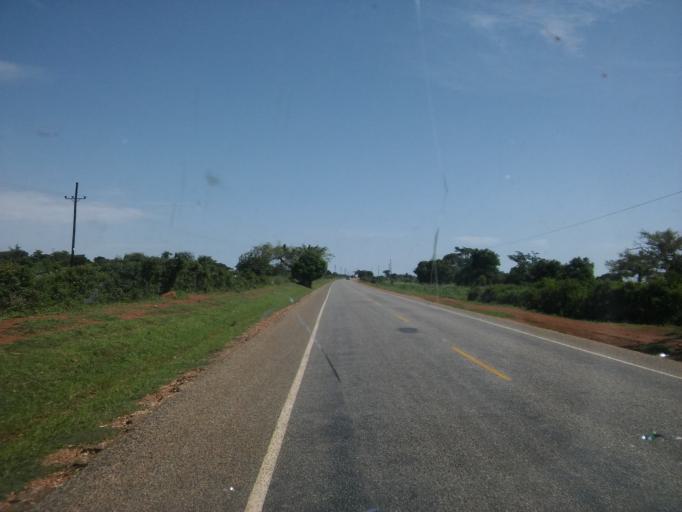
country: UG
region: Eastern Region
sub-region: Bukedea District
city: Bukedea
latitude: 1.3749
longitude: 34.0180
